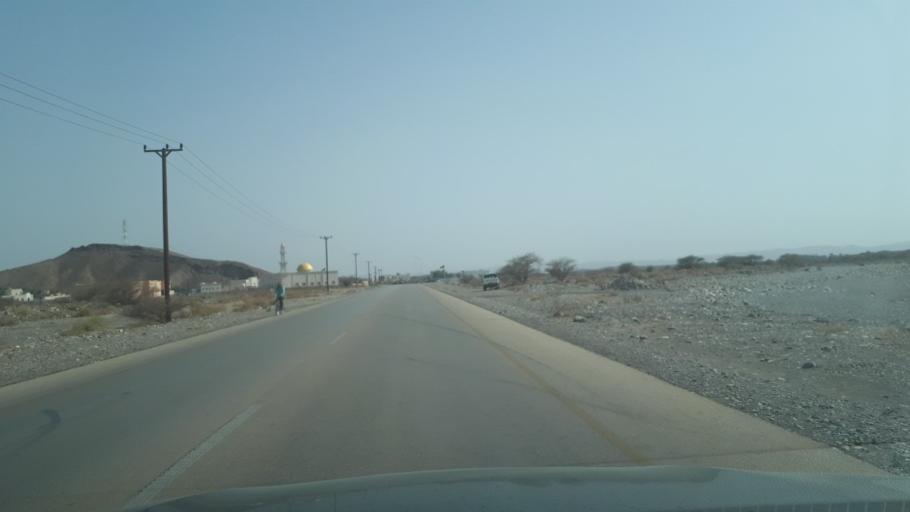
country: OM
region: Az Zahirah
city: `Ibri
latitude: 23.1406
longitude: 56.8937
